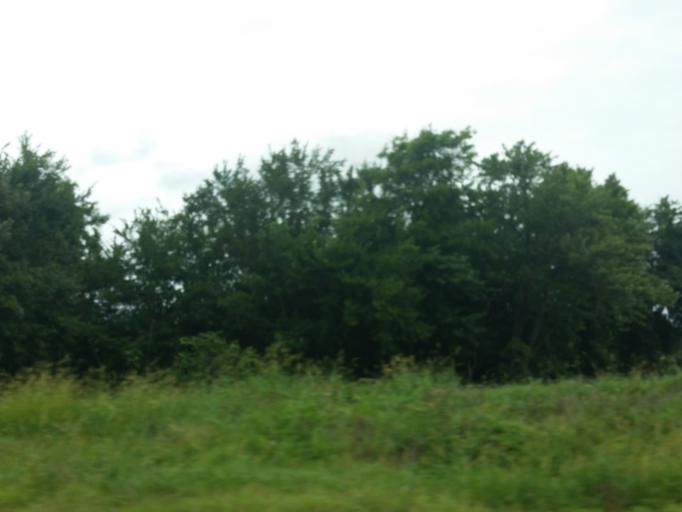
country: US
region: Illinois
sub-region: Alexander County
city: Cairo
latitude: 36.9670
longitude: -89.1560
